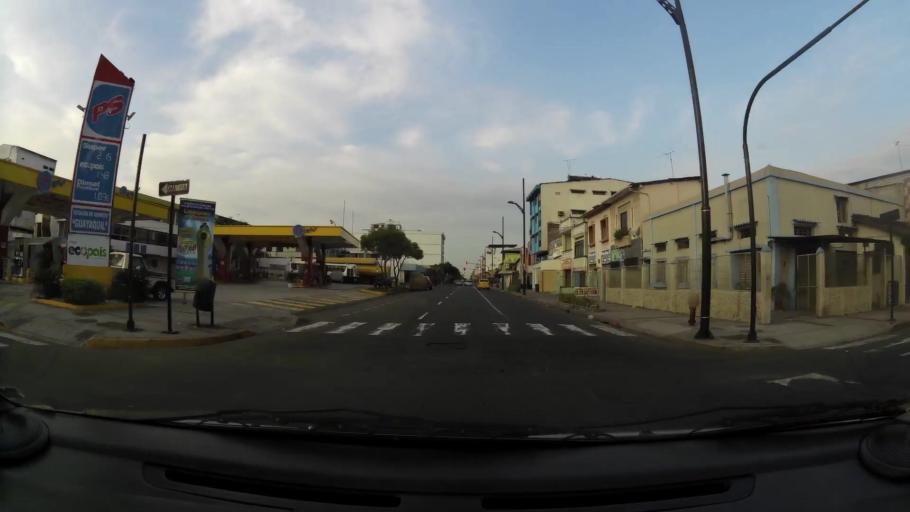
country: EC
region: Guayas
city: Guayaquil
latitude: -2.1918
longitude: -79.8952
